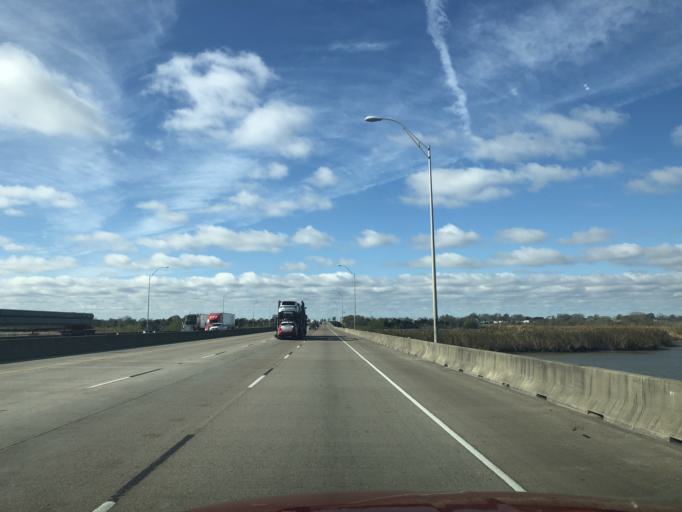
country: US
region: Texas
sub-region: Chambers County
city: Old River-Winfree
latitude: 29.8323
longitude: -94.7921
